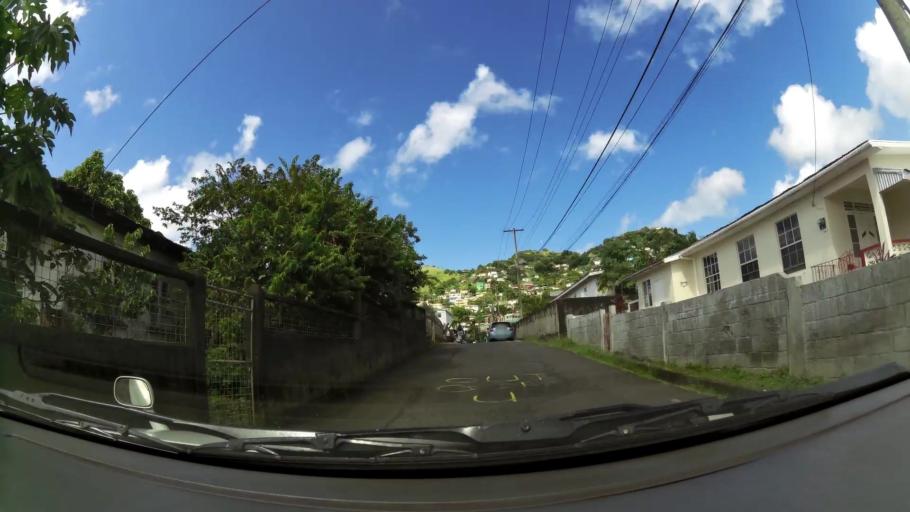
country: VC
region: Saint George
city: Kingstown
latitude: 13.1607
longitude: -61.2284
